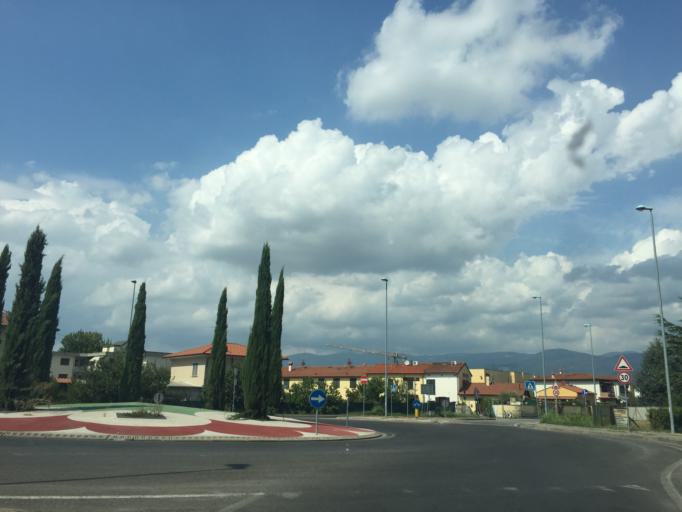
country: IT
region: Tuscany
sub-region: Provincia di Pistoia
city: Barba
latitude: 43.8892
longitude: 10.9635
